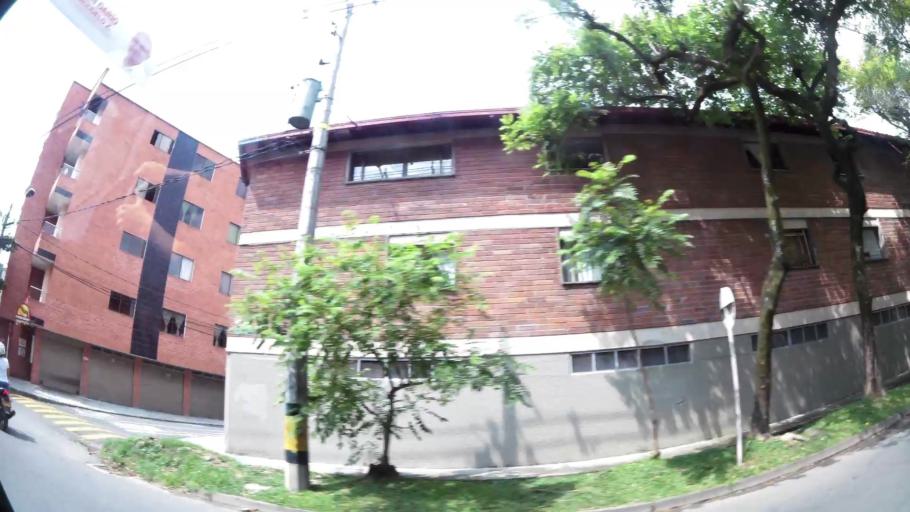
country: CO
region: Antioquia
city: Envigado
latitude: 6.1688
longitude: -75.5937
